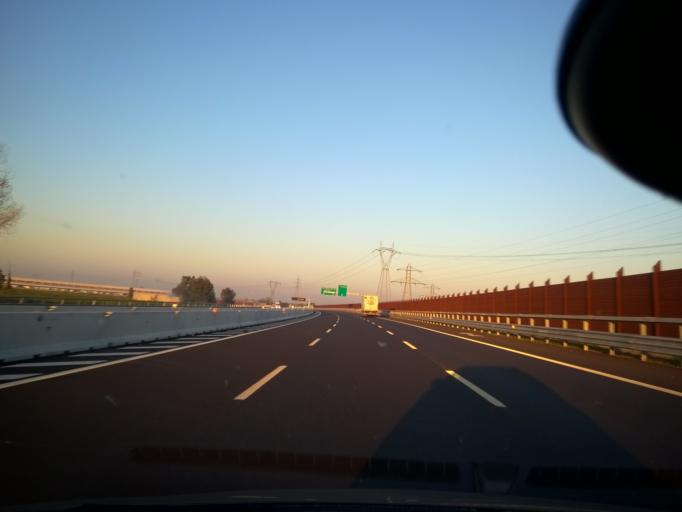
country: IT
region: Lombardy
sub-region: Citta metropolitana di Milano
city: Paullo
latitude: 45.4097
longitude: 9.4112
